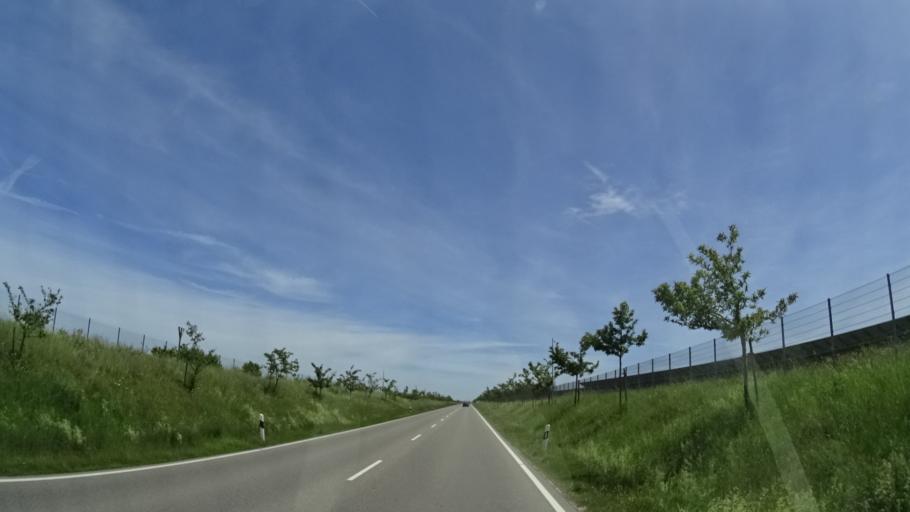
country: DE
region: Baden-Wuerttemberg
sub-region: Regierungsbezirk Stuttgart
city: Schwaebisch Hall
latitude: 49.1177
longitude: 9.7719
